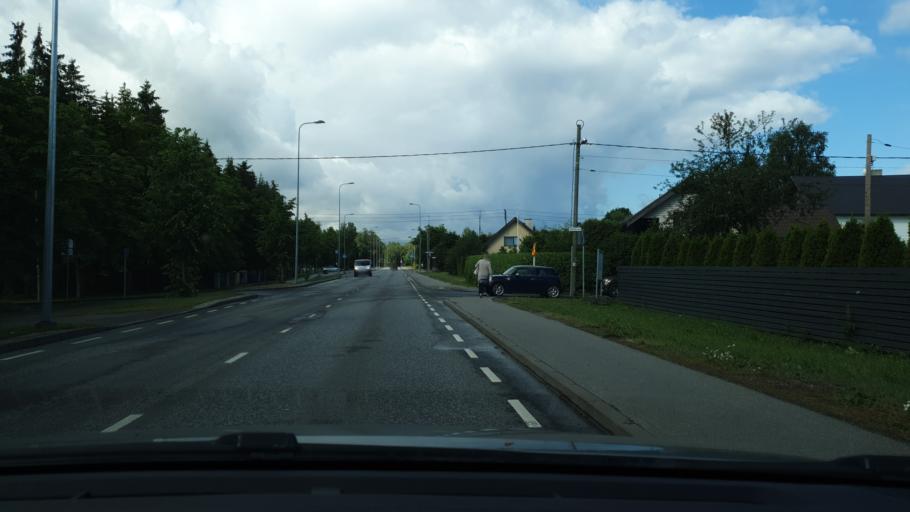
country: EE
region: Harju
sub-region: Viimsi vald
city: Viimsi
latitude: 59.4890
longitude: 24.8732
